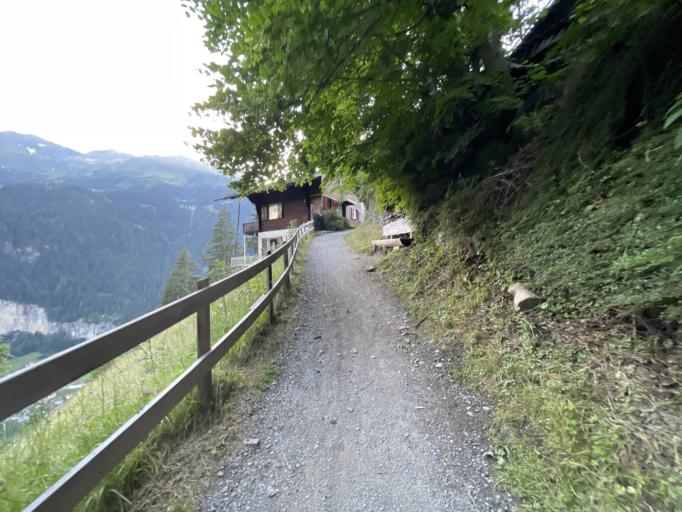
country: CH
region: Bern
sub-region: Interlaken-Oberhasli District
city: Lauterbrunnen
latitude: 46.6006
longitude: 7.9162
